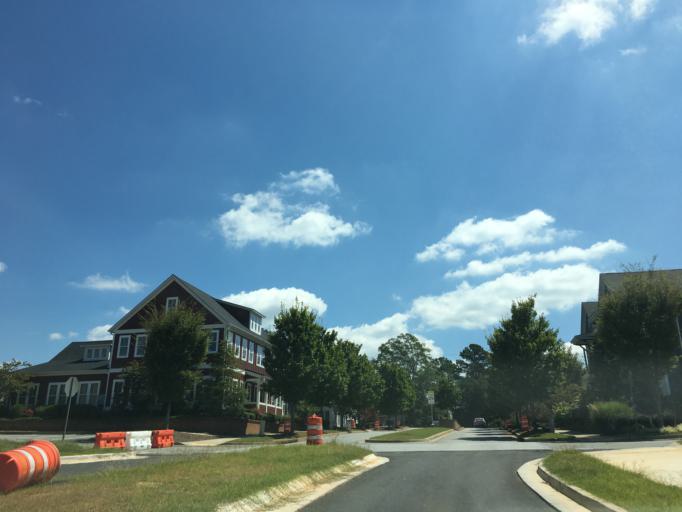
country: US
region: Georgia
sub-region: Fulton County
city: Alpharetta
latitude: 34.0917
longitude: -84.3408
